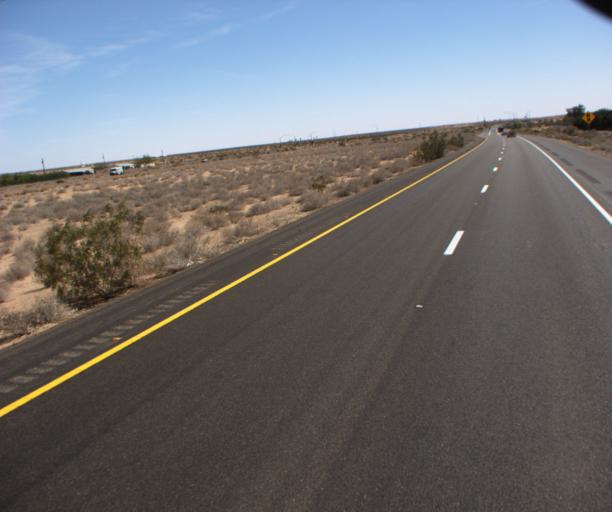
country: US
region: Arizona
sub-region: Yuma County
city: Fortuna Foothills
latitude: 32.6304
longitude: -114.5216
